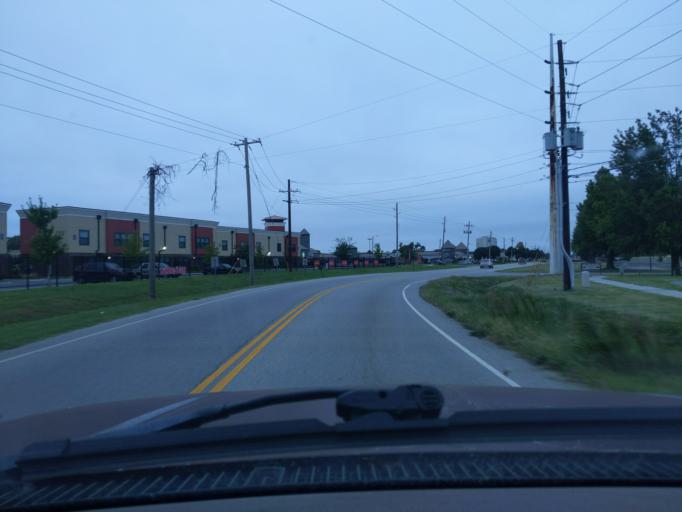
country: US
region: Oklahoma
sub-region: Tulsa County
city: Jenks
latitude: 36.0413
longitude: -95.9576
